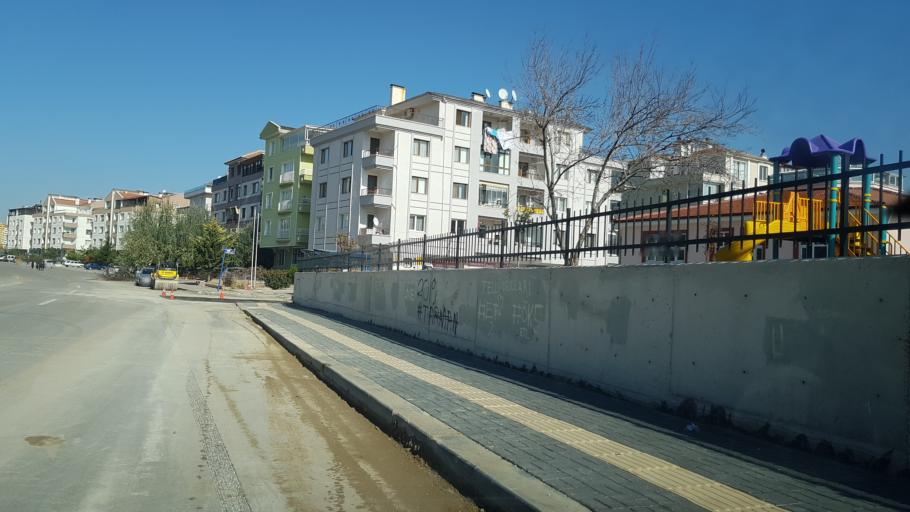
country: TR
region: Ankara
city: Etimesgut
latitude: 39.9737
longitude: 32.6129
